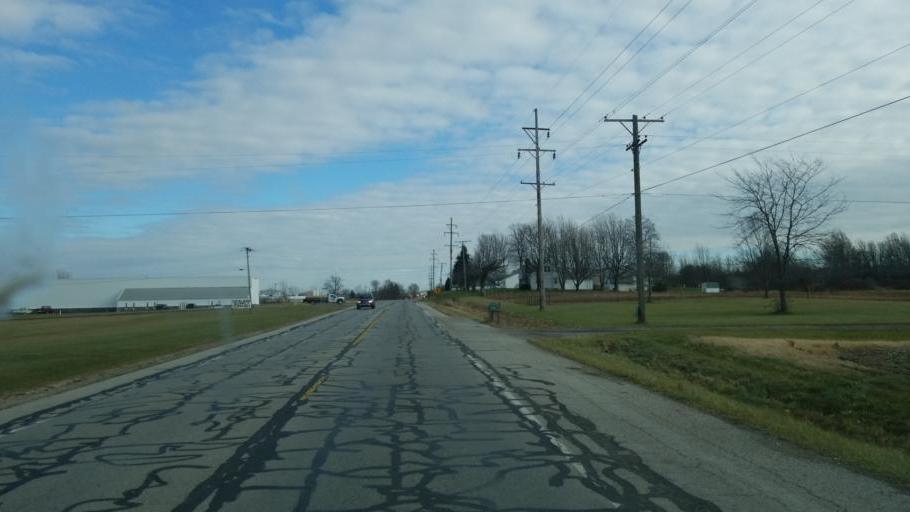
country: US
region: Ohio
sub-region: Crawford County
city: Crestline
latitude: 40.7861
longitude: -82.6931
